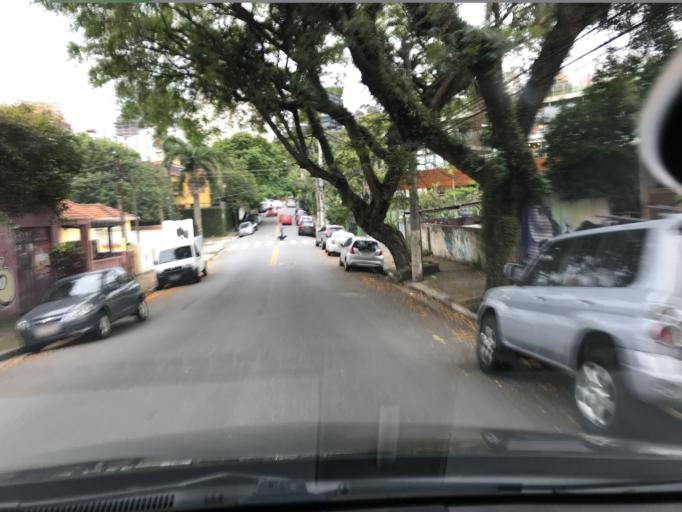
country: BR
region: Sao Paulo
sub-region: Sao Paulo
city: Sao Paulo
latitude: -23.5509
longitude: -46.6965
